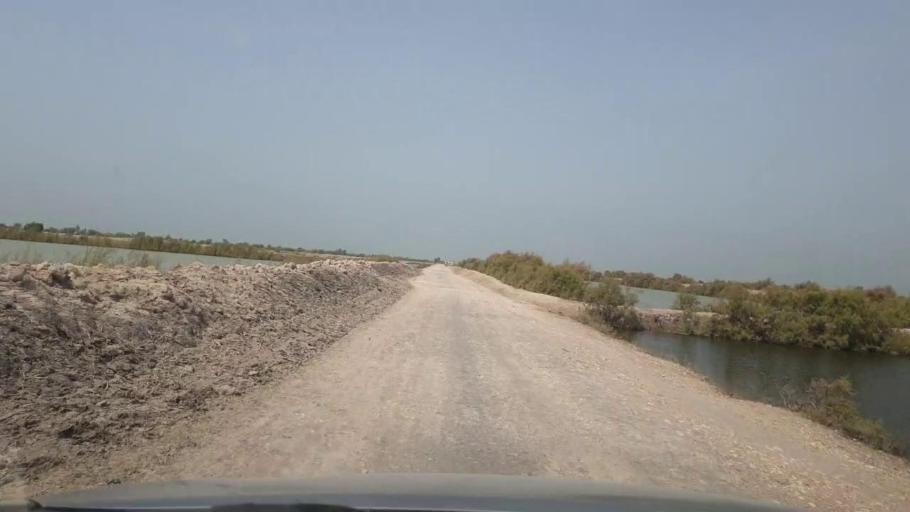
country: PK
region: Sindh
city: Garhi Yasin
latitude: 27.9133
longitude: 68.4133
